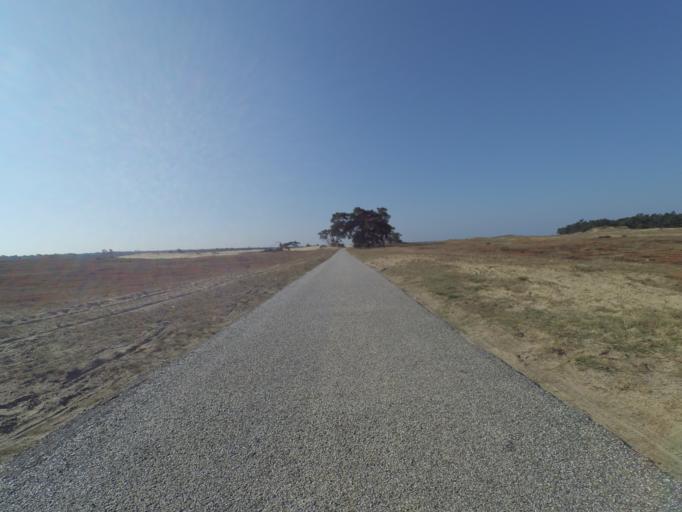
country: NL
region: Gelderland
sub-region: Gemeente Ede
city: Otterlo
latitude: 52.0783
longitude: 5.8271
